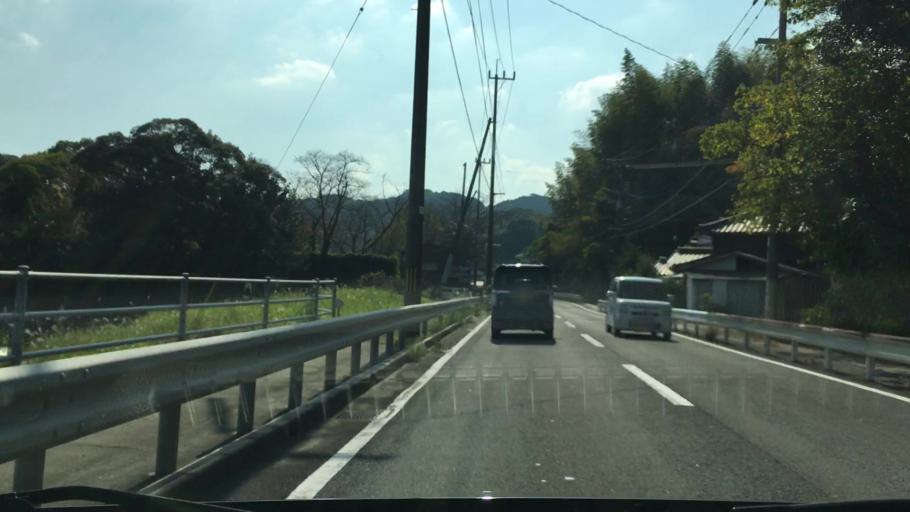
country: JP
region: Nagasaki
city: Togitsu
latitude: 32.9356
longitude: 129.7839
